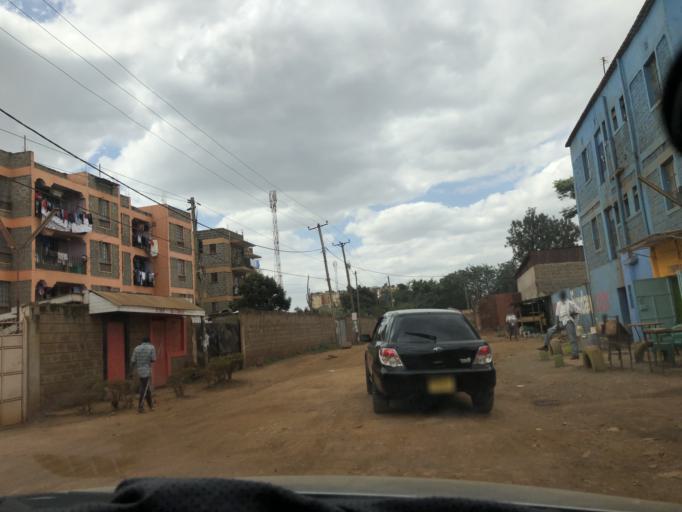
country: KE
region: Nairobi Area
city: Pumwani
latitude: -1.2312
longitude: 36.8761
